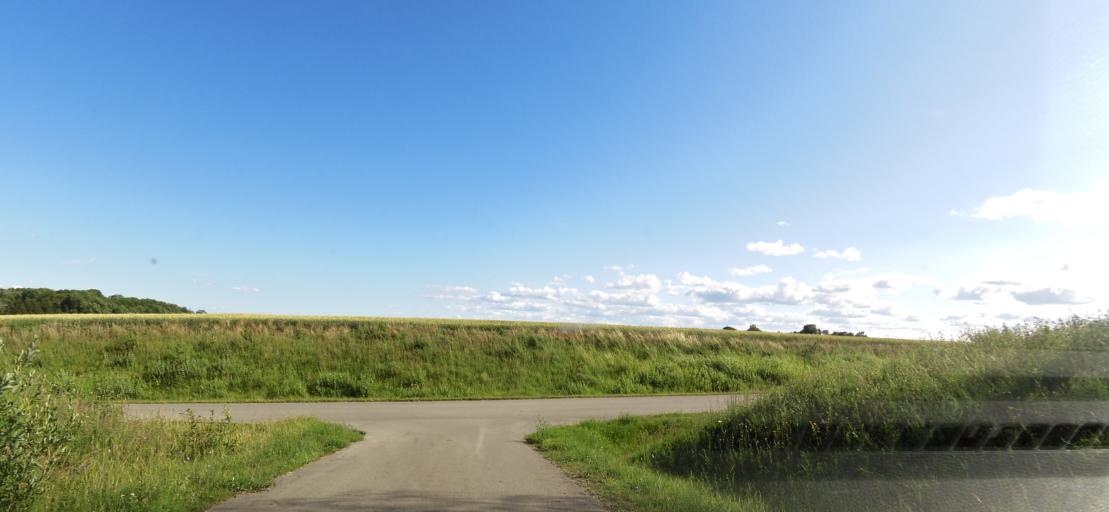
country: LT
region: Panevezys
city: Pasvalys
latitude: 56.1526
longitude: 24.4477
